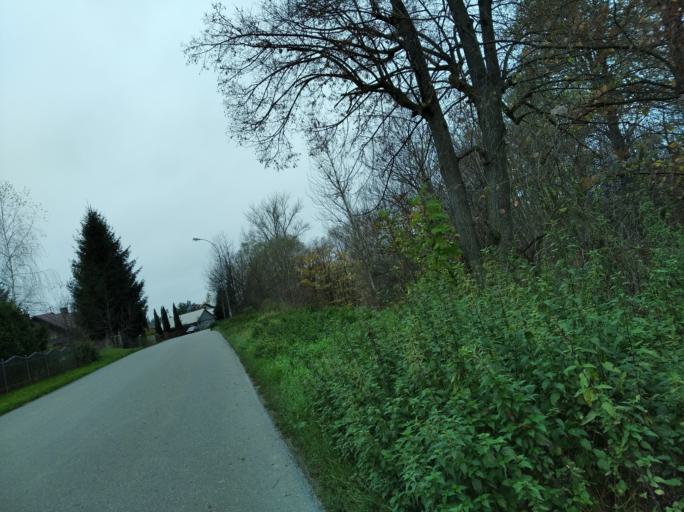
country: PL
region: Subcarpathian Voivodeship
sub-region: Powiat krosnienski
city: Jedlicze
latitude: 49.6945
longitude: 21.6612
